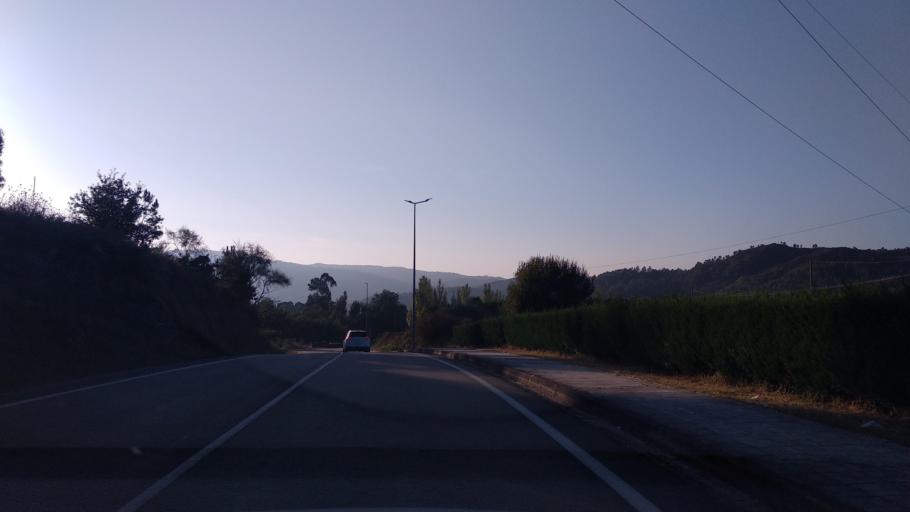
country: ES
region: Galicia
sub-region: Provincia de Pontevedra
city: Redondela
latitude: 42.3397
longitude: -8.5901
